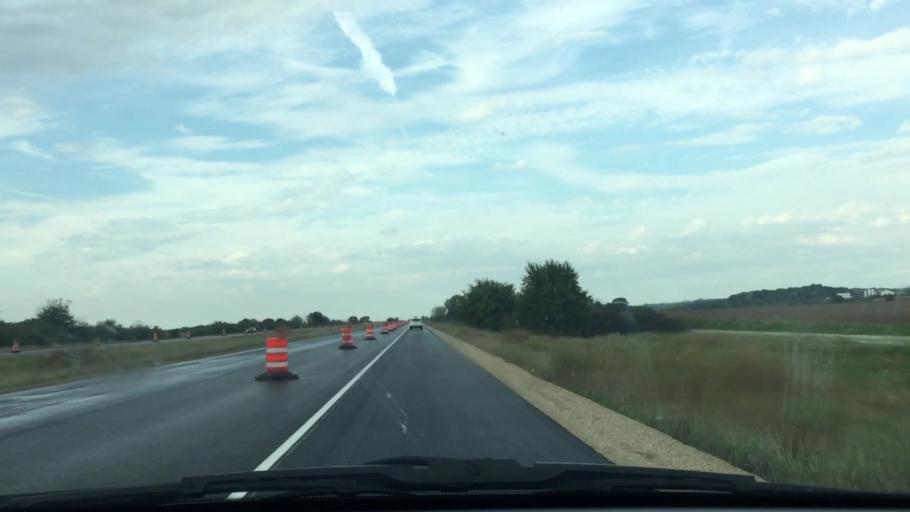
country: US
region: Illinois
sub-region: Whiteside County
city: Erie
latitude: 41.7110
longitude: -90.0146
